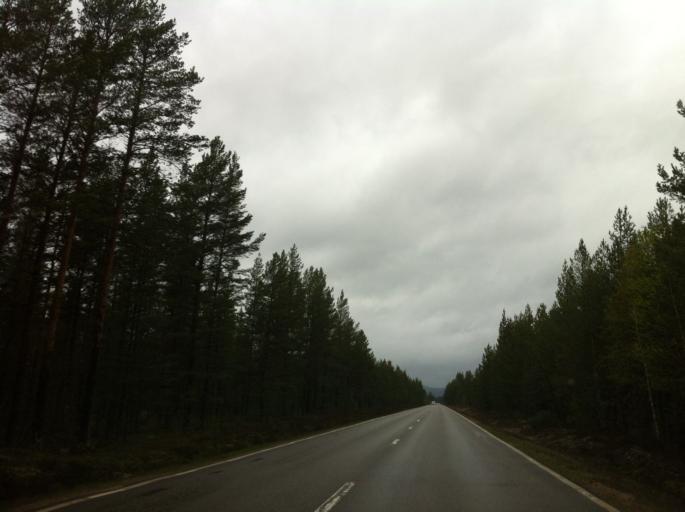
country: SE
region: Jaemtland
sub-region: Harjedalens Kommun
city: Sveg
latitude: 62.1352
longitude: 14.0039
